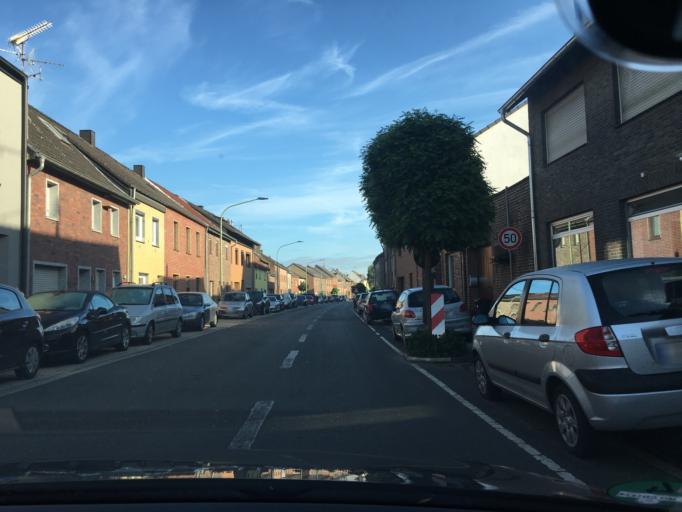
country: DE
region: North Rhine-Westphalia
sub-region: Regierungsbezirk Koln
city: Niederzier
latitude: 50.8986
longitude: 6.4464
